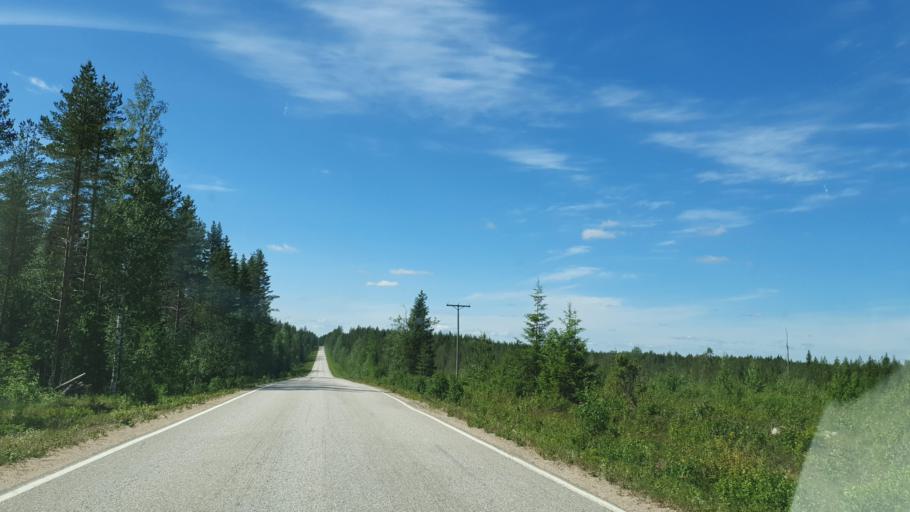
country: FI
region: Kainuu
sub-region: Kehys-Kainuu
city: Suomussalmi
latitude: 64.5853
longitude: 29.0588
